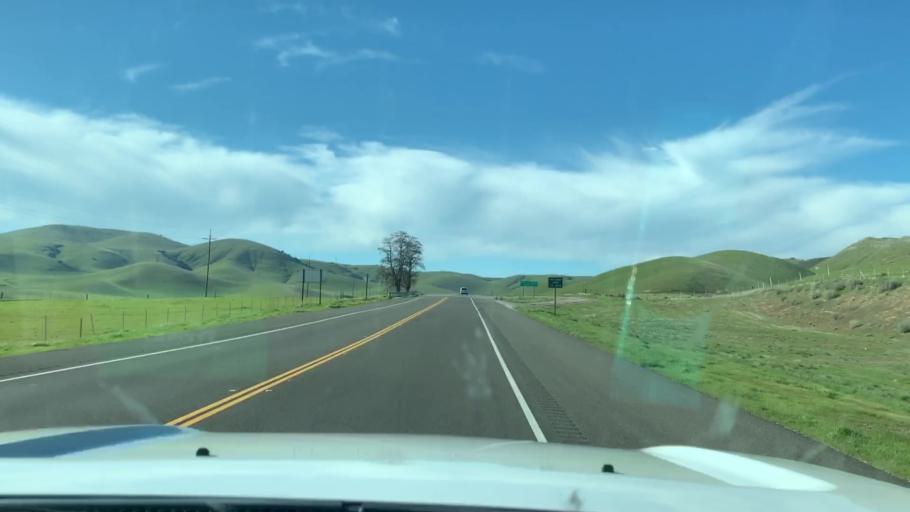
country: US
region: California
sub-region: San Luis Obispo County
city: Shandon
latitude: 35.7252
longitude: -120.1928
